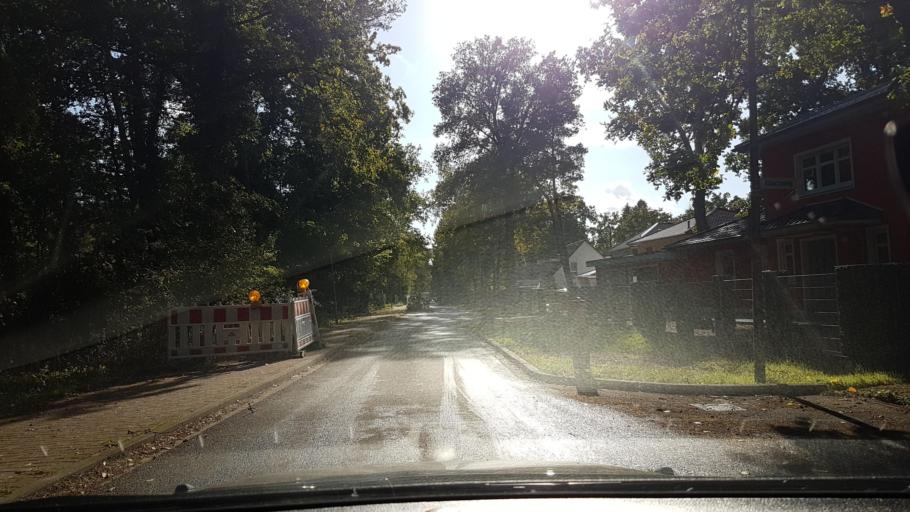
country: DE
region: Lower Saxony
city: Isernhagen Farster Bauerschaft
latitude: 52.5192
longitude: 9.7843
